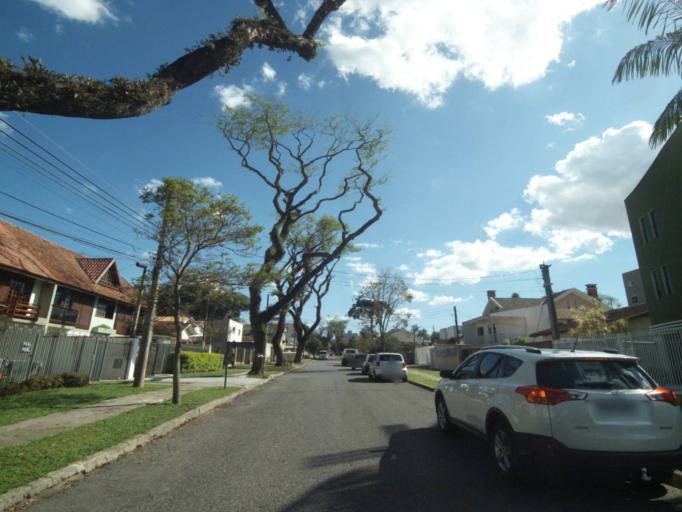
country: BR
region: Parana
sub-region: Curitiba
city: Curitiba
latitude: -25.3934
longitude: -49.2469
